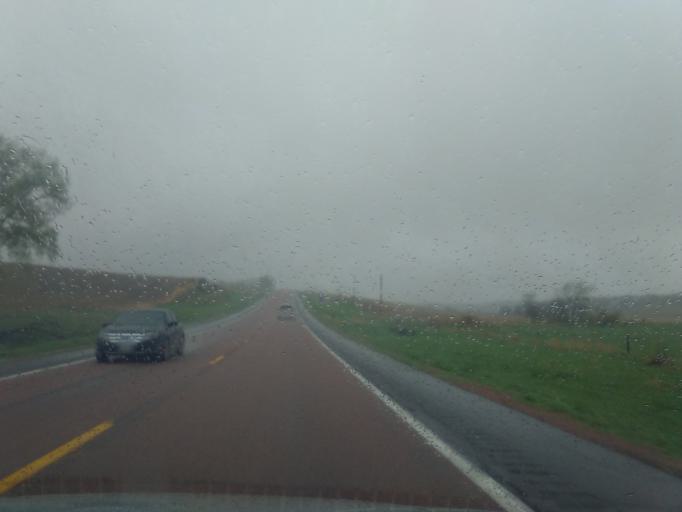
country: US
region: Nebraska
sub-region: Wayne County
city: Wayne
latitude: 42.2356
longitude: -97.1272
